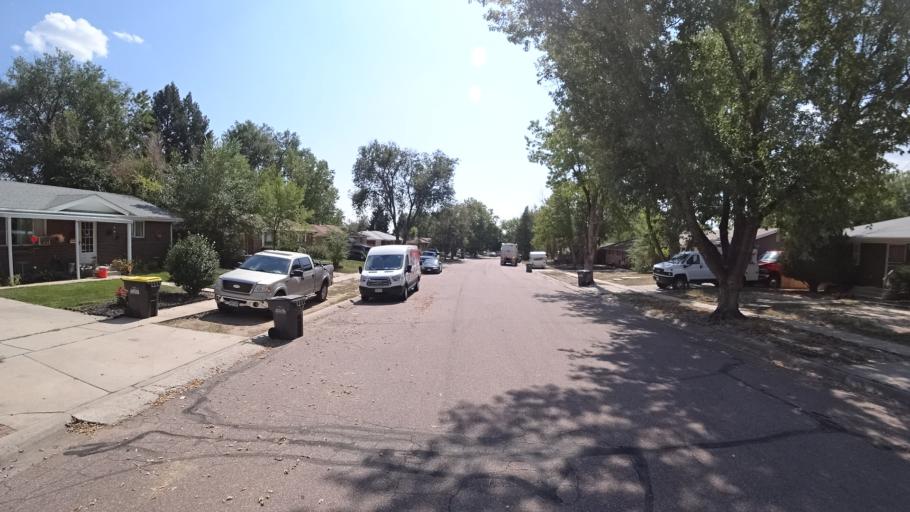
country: US
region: Colorado
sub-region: El Paso County
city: Colorado Springs
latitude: 38.8342
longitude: -104.7685
